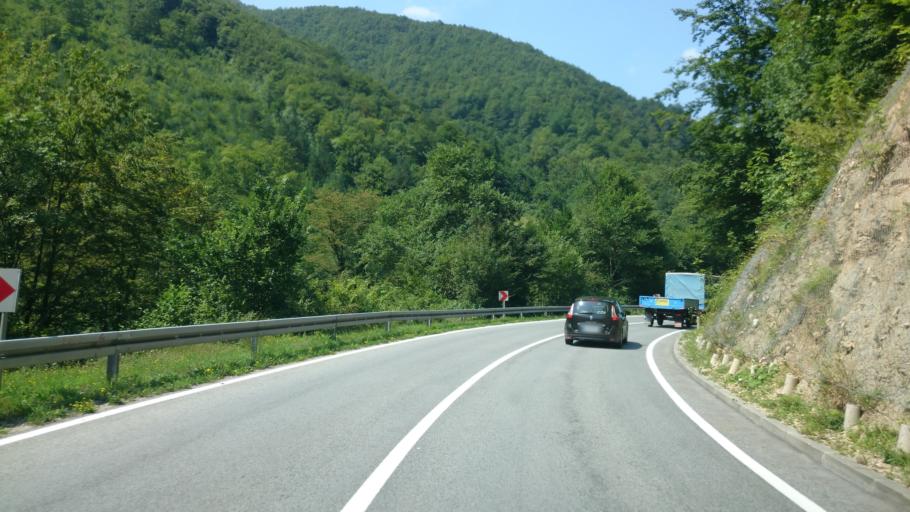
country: BA
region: Federation of Bosnia and Herzegovina
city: Donji Vakuf
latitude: 44.2165
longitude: 17.3133
